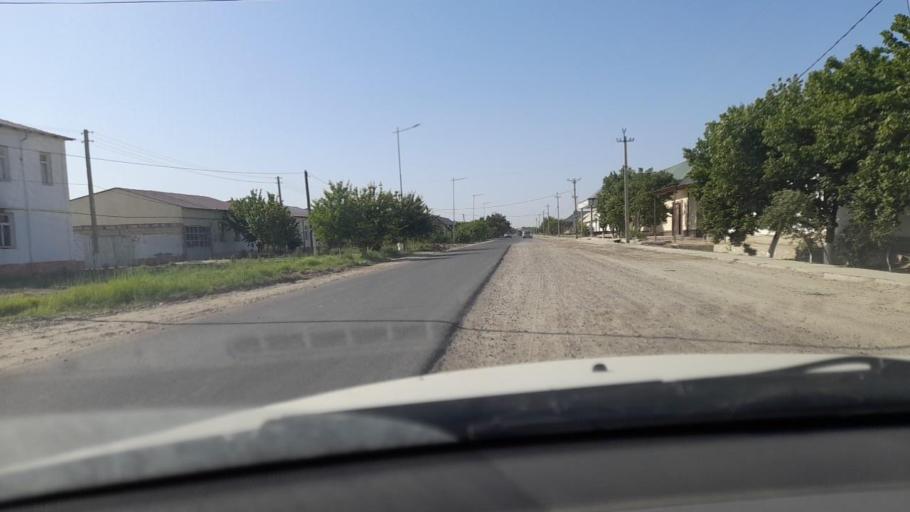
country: UZ
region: Bukhara
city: Romiton
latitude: 40.0754
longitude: 64.3262
